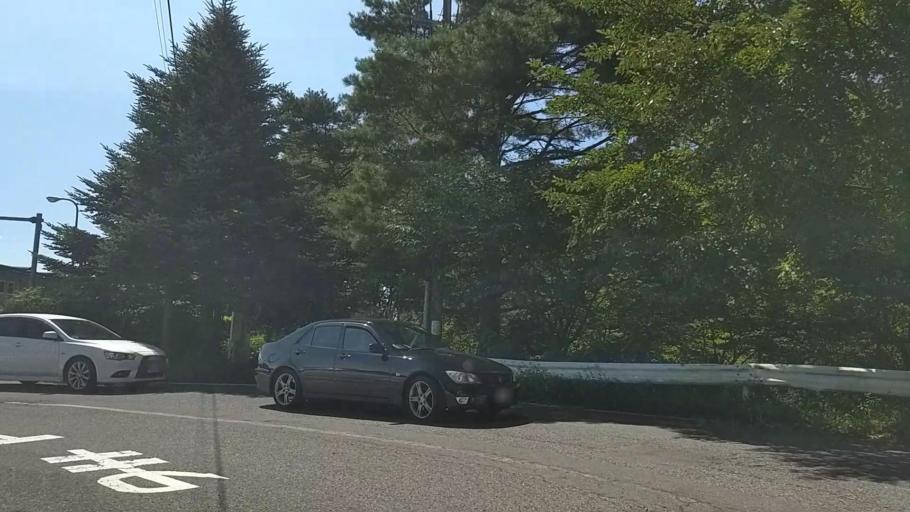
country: JP
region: Nagano
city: Saku
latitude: 36.3414
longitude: 138.6304
